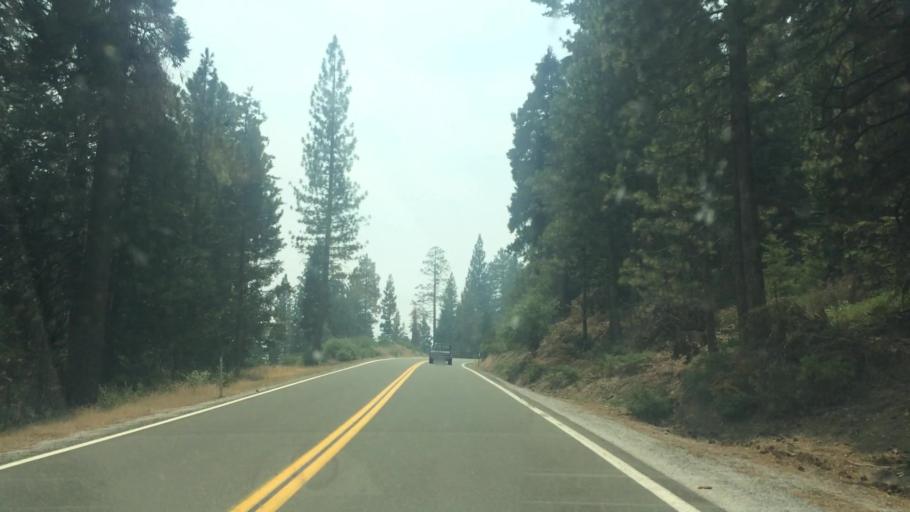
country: US
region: California
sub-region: Amador County
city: Pioneer
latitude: 38.5421
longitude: -120.3814
